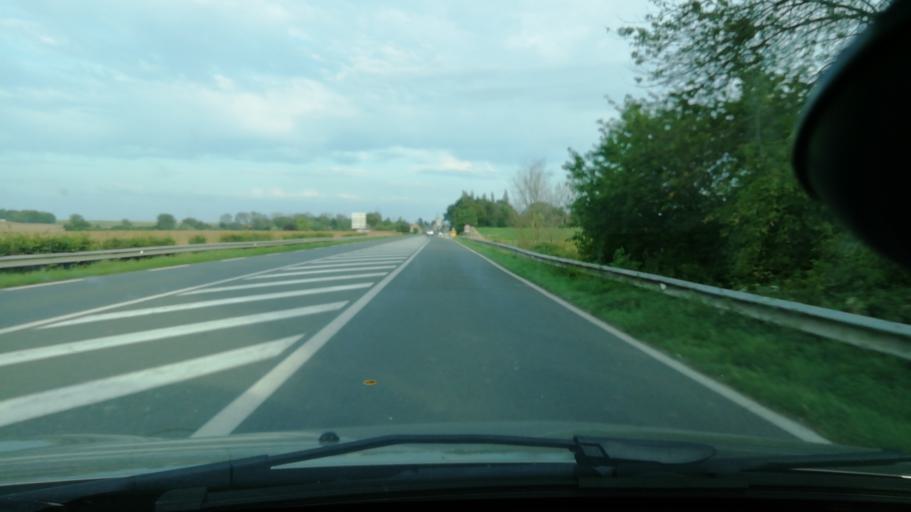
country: FR
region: Nord-Pas-de-Calais
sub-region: Departement du Nord
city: Viesly
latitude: 50.1264
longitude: 3.4447
